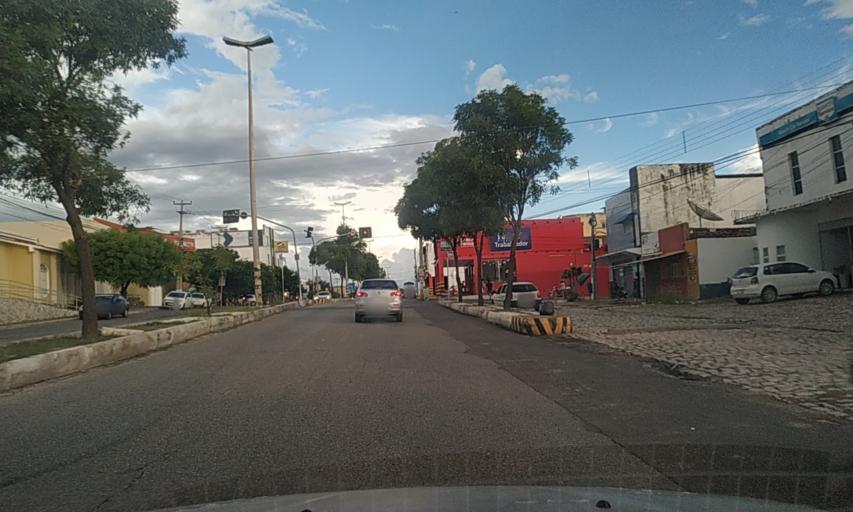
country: BR
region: Rio Grande do Norte
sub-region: Mossoro
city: Mossoro
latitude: -5.2064
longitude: -37.3356
